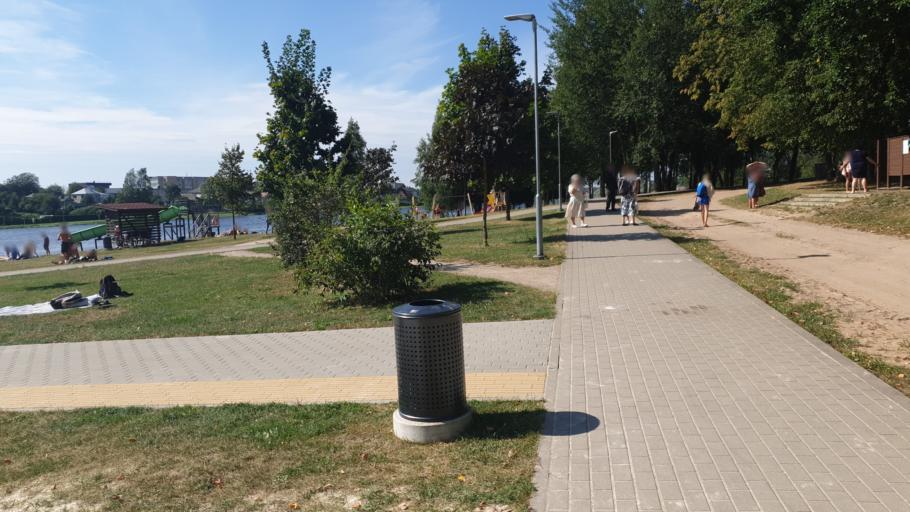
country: LT
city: Sirvintos
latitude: 55.0434
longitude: 24.9609
